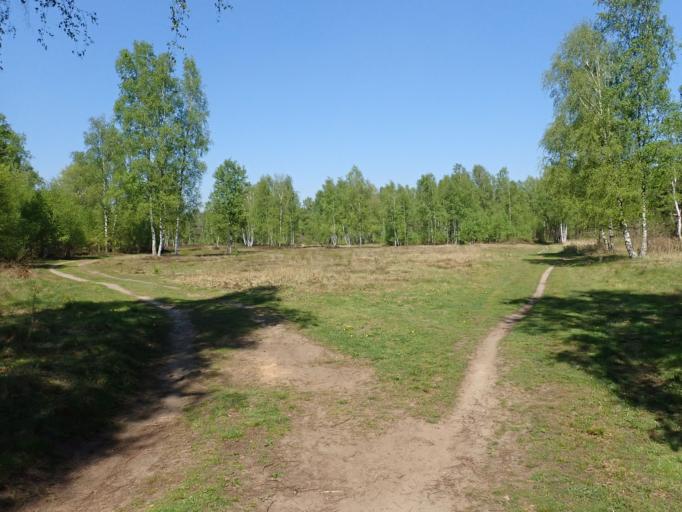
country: BE
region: Flanders
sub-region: Provincie Antwerpen
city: Brasschaat
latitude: 51.3392
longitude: 4.5125
